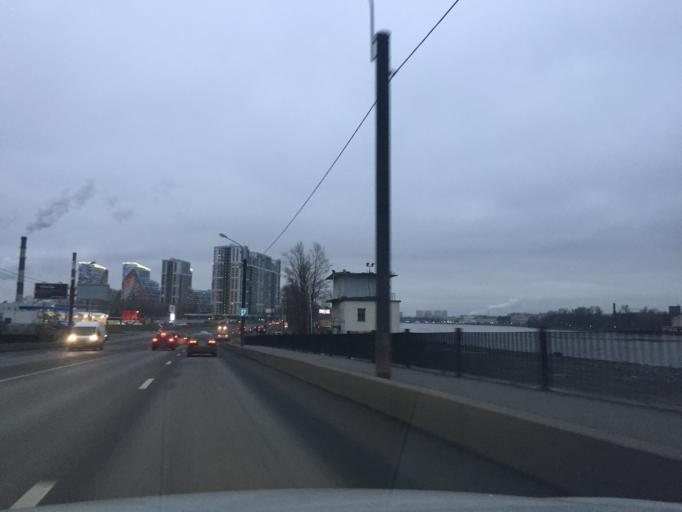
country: RU
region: St.-Petersburg
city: Obukhovo
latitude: 59.8995
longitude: 30.4428
